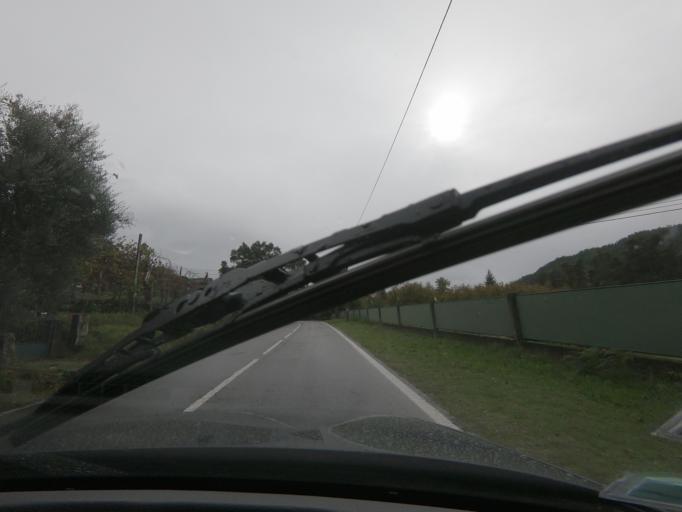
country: PT
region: Vila Real
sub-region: Mondim de Basto
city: Mondim de Basto
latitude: 41.3721
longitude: -7.9353
